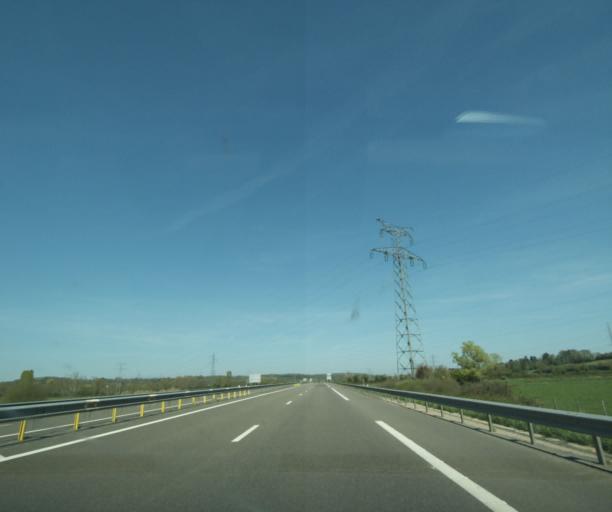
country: FR
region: Bourgogne
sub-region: Departement de la Nievre
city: Coulanges-les-Nevers
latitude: 46.9965
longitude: 3.2057
